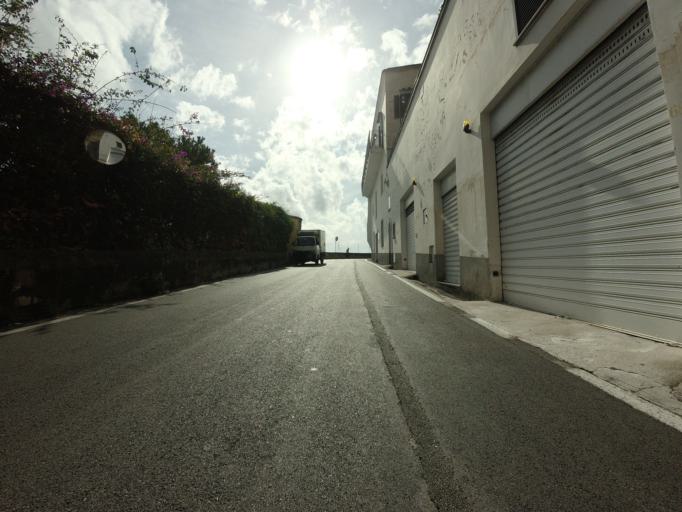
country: IT
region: Campania
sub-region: Provincia di Salerno
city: Positano
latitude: 40.6278
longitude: 14.4917
